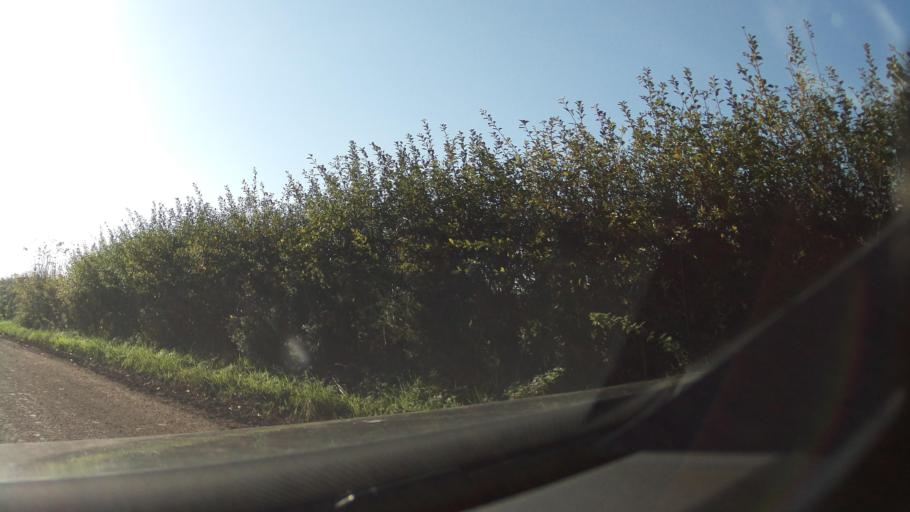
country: GB
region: England
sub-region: Somerset
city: Castle Cary
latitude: 51.0496
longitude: -2.4822
